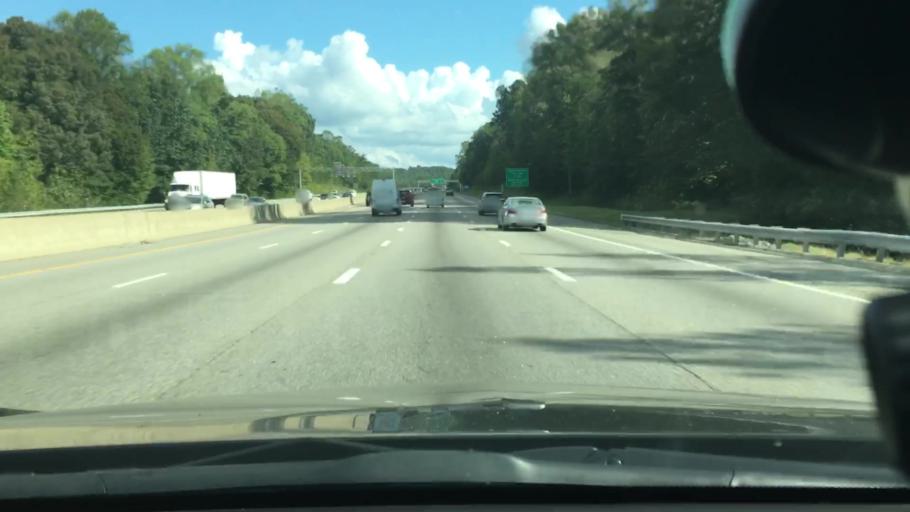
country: US
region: North Carolina
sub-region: Orange County
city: Hillsborough
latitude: 36.0657
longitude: -79.1439
